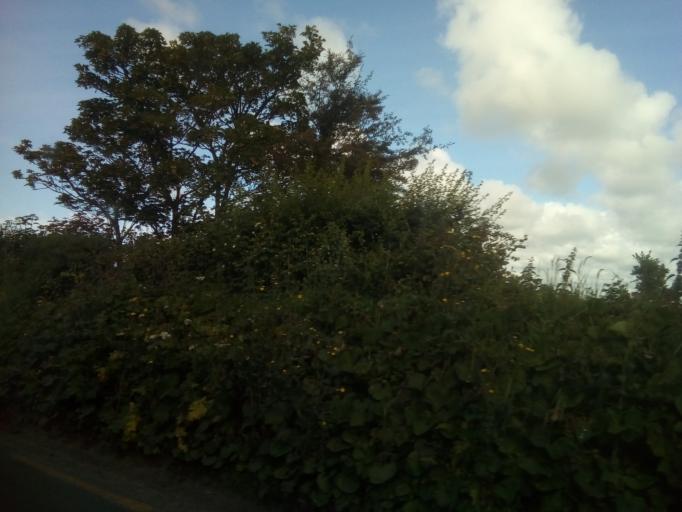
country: IE
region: Leinster
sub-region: Loch Garman
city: Loch Garman
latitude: 52.2367
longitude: -6.5533
